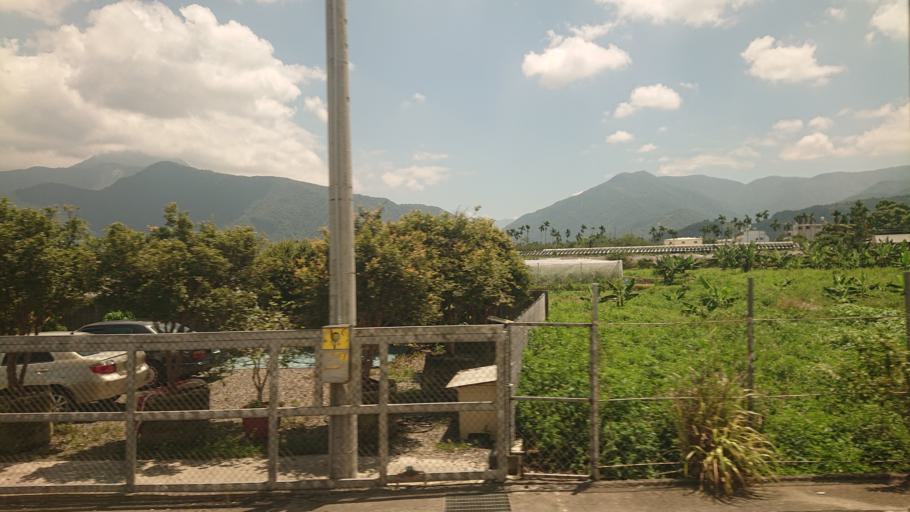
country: TW
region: Taiwan
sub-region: Nantou
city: Puli
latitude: 23.9753
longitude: 120.9623
